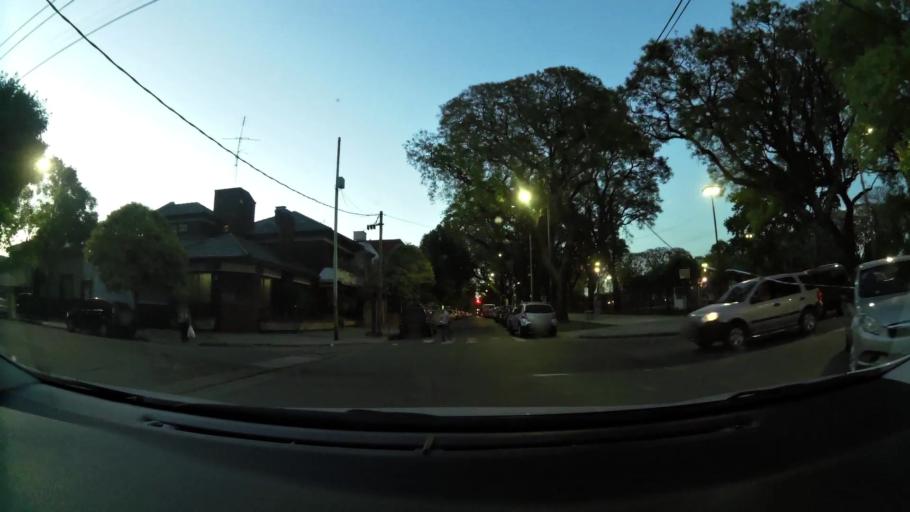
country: AR
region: Buenos Aires F.D.
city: Villa Lugano
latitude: -34.6892
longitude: -58.4749
